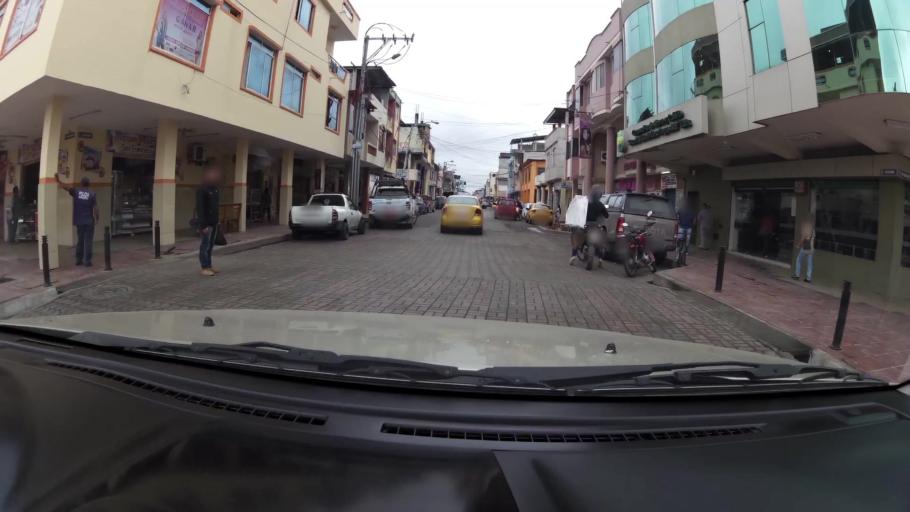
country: EC
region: El Oro
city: Pasaje
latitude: -3.3277
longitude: -79.8101
